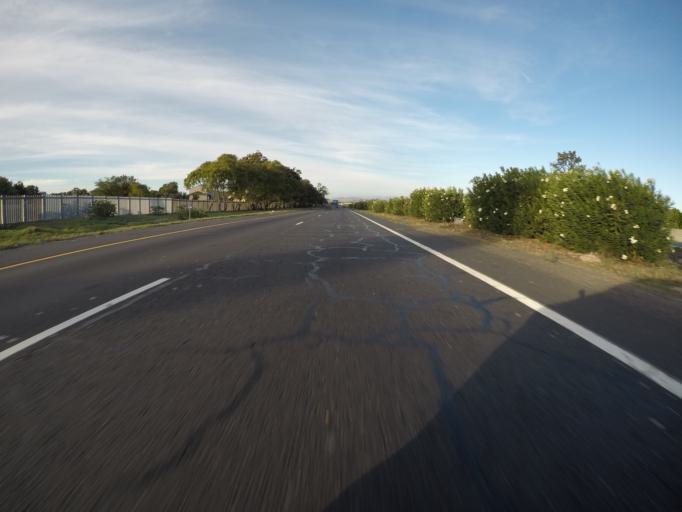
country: ZA
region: Western Cape
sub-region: City of Cape Town
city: Kraaifontein
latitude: -33.8509
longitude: 18.7063
